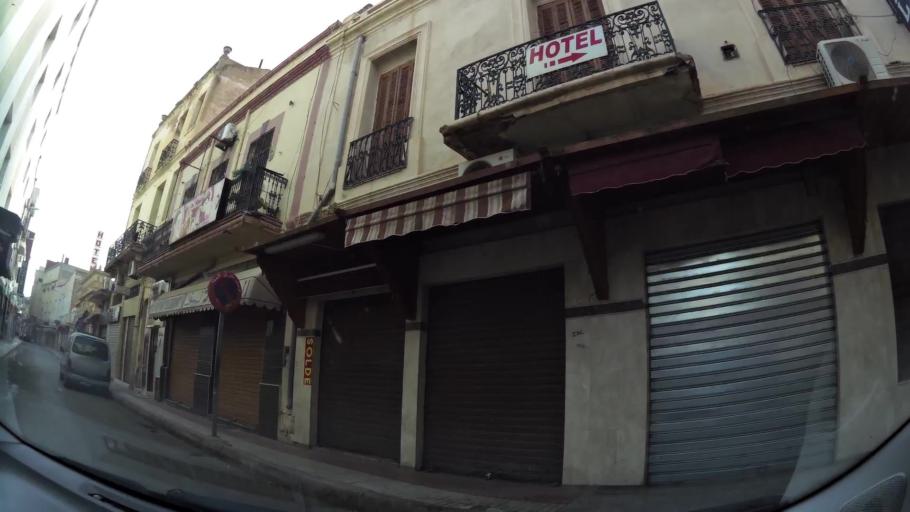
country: MA
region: Oriental
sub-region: Oujda-Angad
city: Oujda
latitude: 34.6815
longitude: -1.9153
